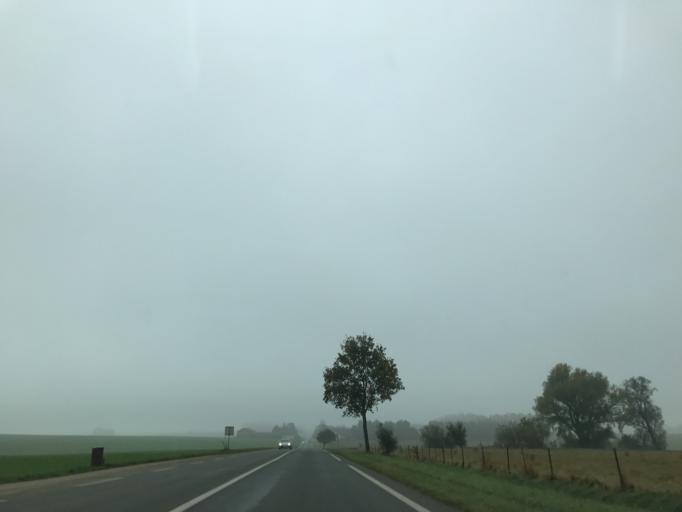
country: FR
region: Nord-Pas-de-Calais
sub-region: Departement du Pas-de-Calais
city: Bapaume
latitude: 50.0716
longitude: 2.8857
